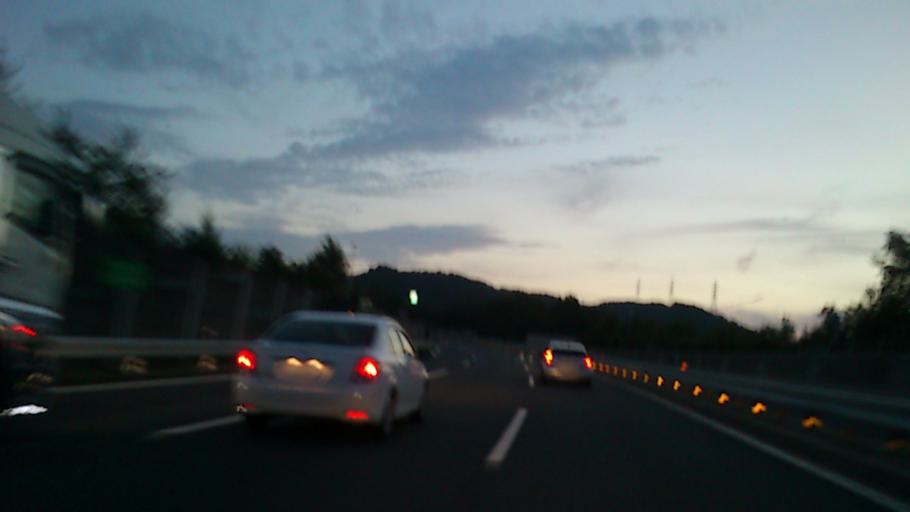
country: JP
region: Gifu
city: Tajimi
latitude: 35.3418
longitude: 137.0930
